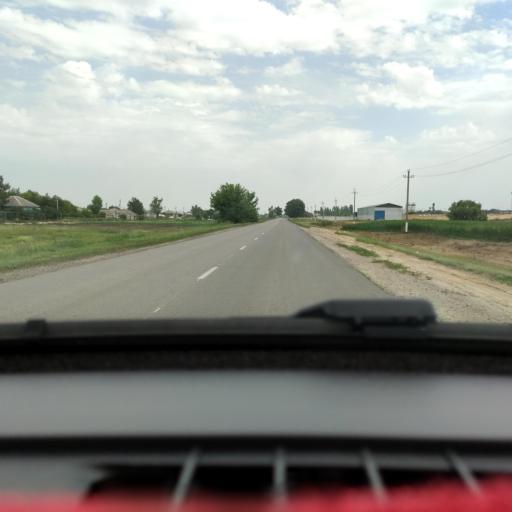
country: RU
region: Voronezj
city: Davydovka
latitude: 51.2250
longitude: 39.5307
